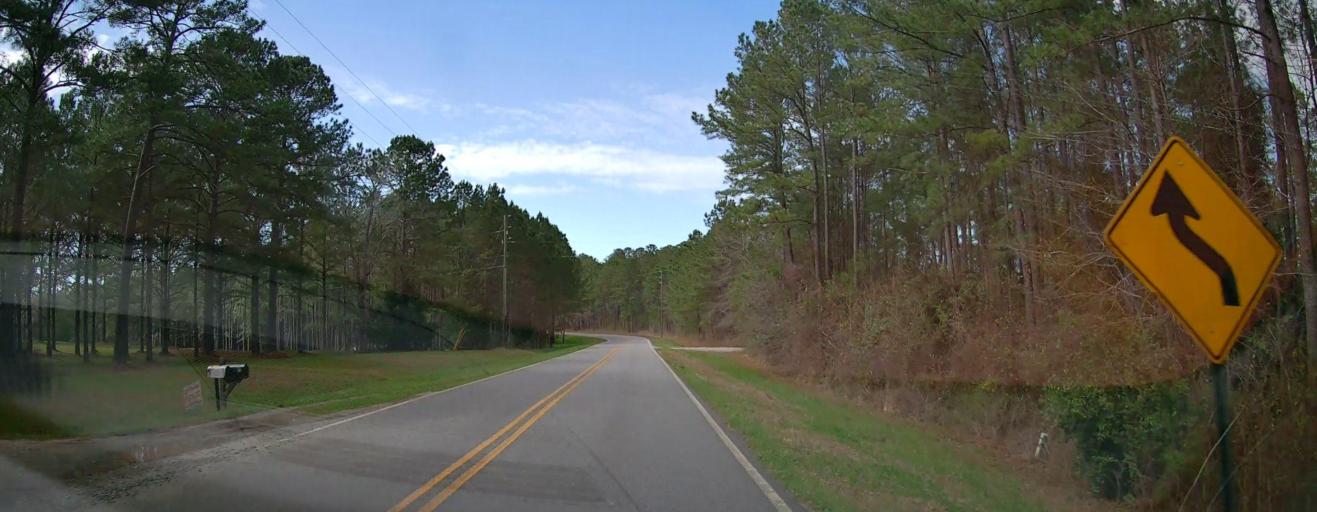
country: US
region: Georgia
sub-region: Jones County
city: Gray
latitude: 33.0623
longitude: -83.7258
